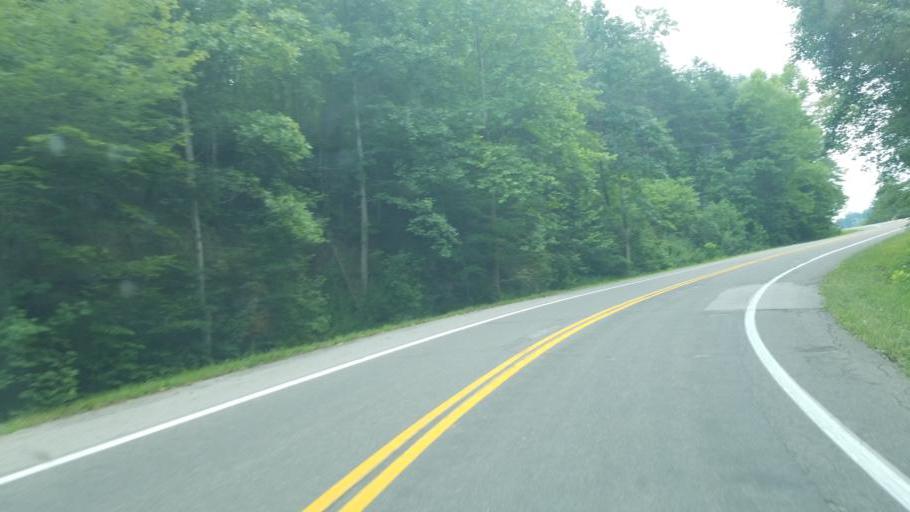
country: US
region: West Virginia
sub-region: Kanawha County
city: Alum Creek
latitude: 38.2797
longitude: -81.7751
